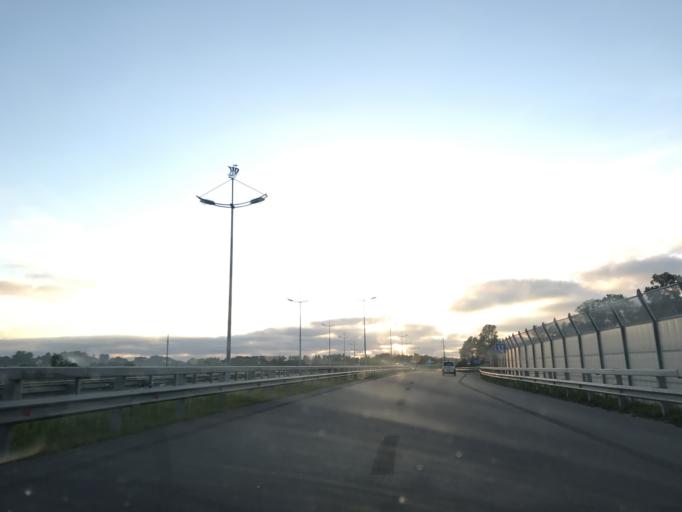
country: RU
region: Kaliningrad
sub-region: Gorod Svetlogorsk
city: Svetlogorsk
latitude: 54.9166
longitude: 20.1927
